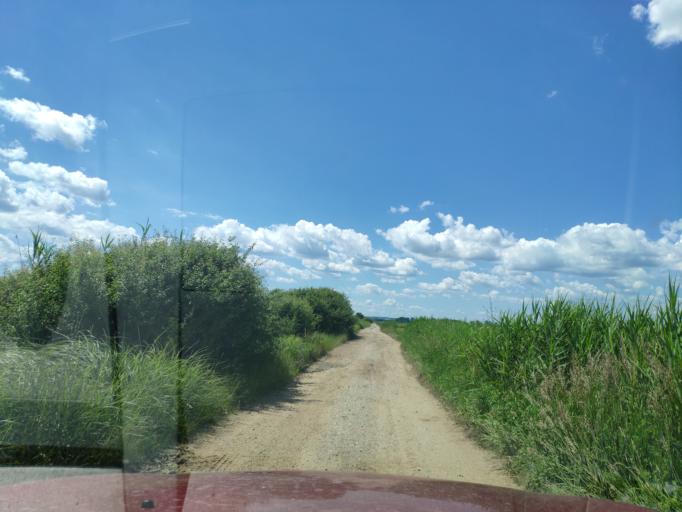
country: HU
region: Borsod-Abauj-Zemplen
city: Ozd
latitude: 48.2844
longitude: 20.2097
